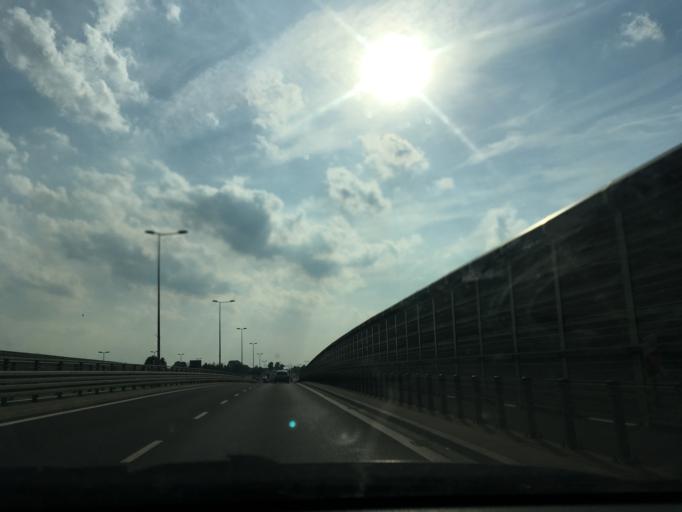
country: PL
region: Podlasie
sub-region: Bialystok
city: Bialystok
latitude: 53.1558
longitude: 23.0869
